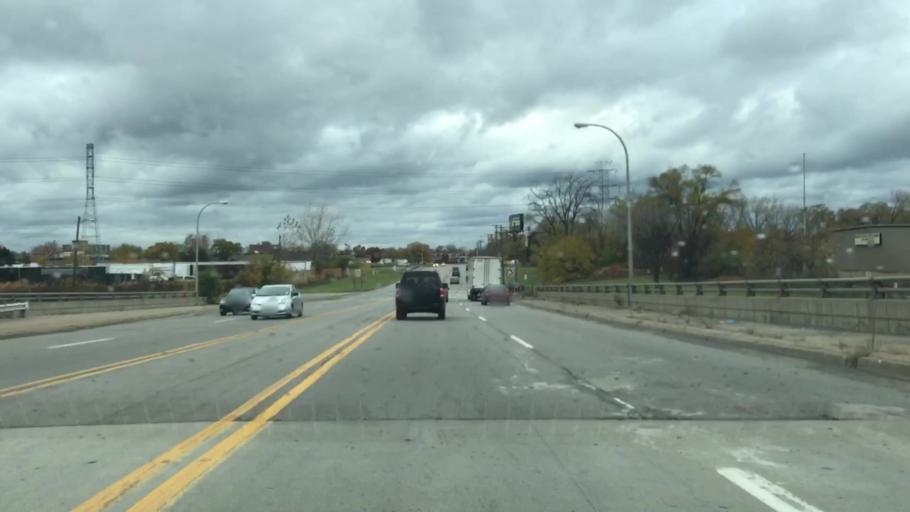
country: US
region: Michigan
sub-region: Wayne County
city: Dearborn
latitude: 42.3183
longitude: -83.1635
